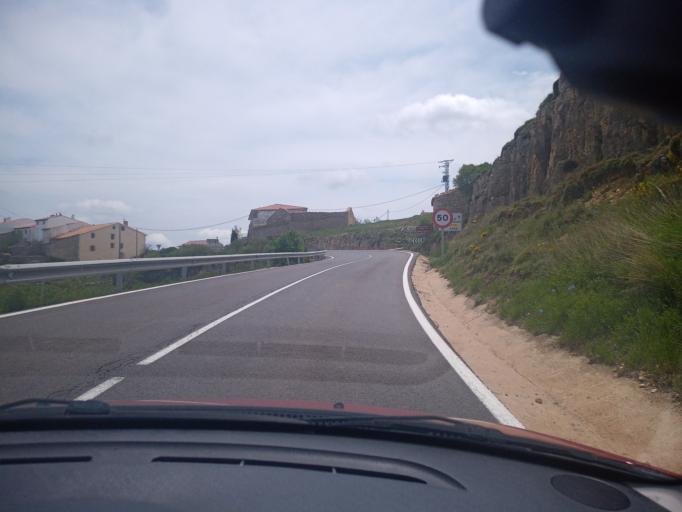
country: ES
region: Valencia
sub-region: Provincia de Castello
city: Ares del Maestre
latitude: 40.4550
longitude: -0.1436
